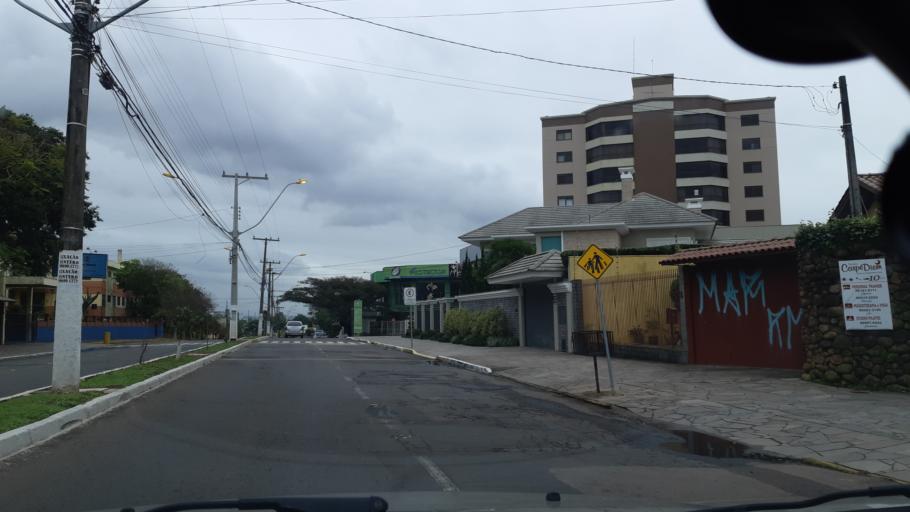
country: BR
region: Rio Grande do Sul
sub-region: Sapucaia Do Sul
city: Sapucaia
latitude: -29.8492
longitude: -51.1609
